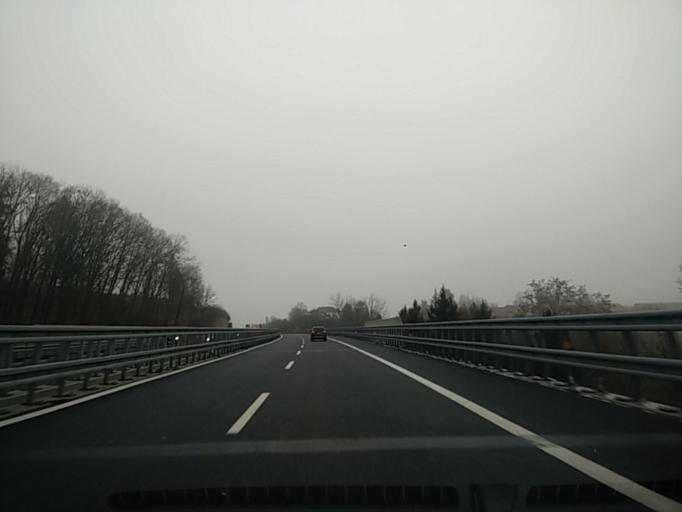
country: IT
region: Piedmont
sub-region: Provincia di Asti
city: Asti
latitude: 44.9159
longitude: 8.2105
